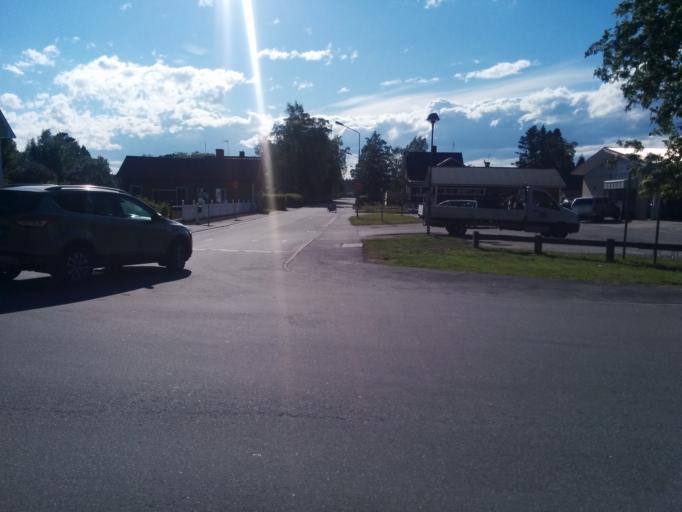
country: SE
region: Vaesterbotten
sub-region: Umea Kommun
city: Hoernefors
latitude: 63.6260
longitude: 19.9086
